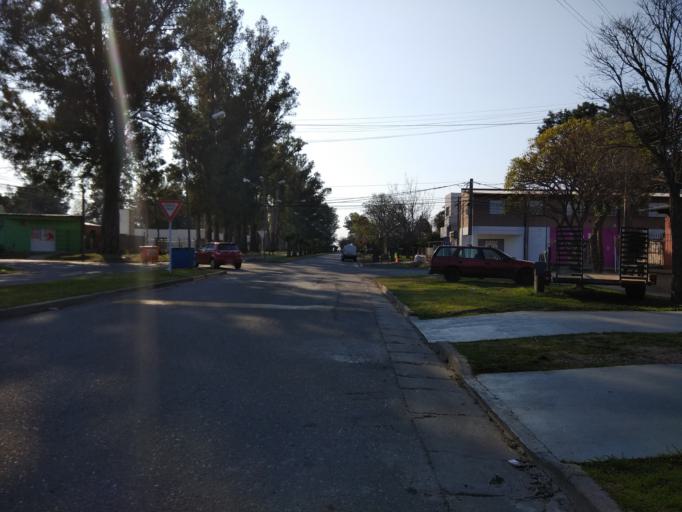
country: AR
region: Santa Fe
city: Granadero Baigorria
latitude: -32.8474
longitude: -60.7023
